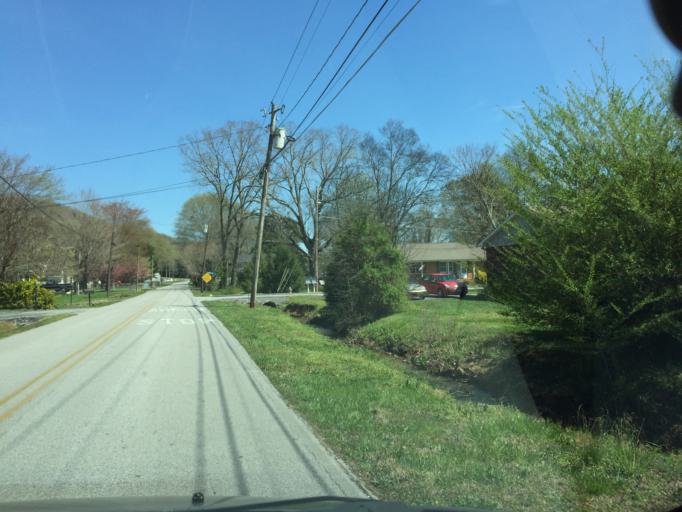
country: US
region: Tennessee
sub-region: Hamilton County
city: Soddy-Daisy
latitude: 35.2299
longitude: -85.2153
